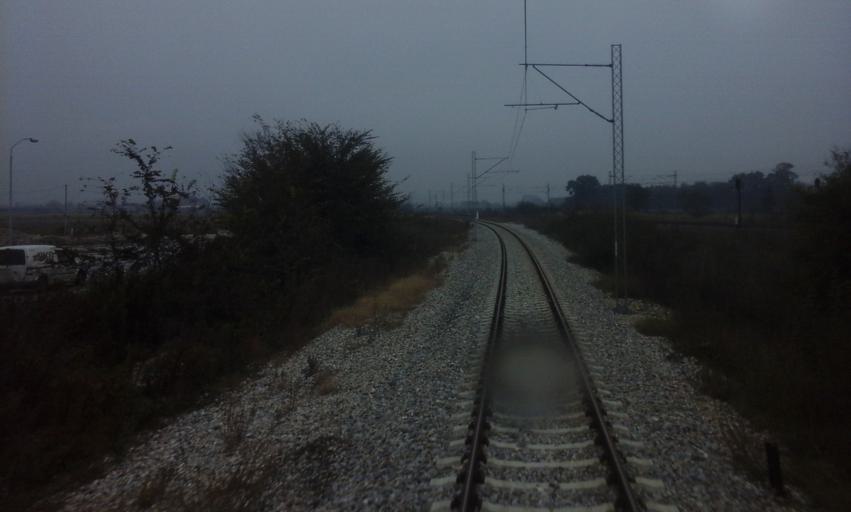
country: RS
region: Central Serbia
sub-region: Pomoravski Okrug
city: Paracin
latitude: 43.8871
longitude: 21.3832
